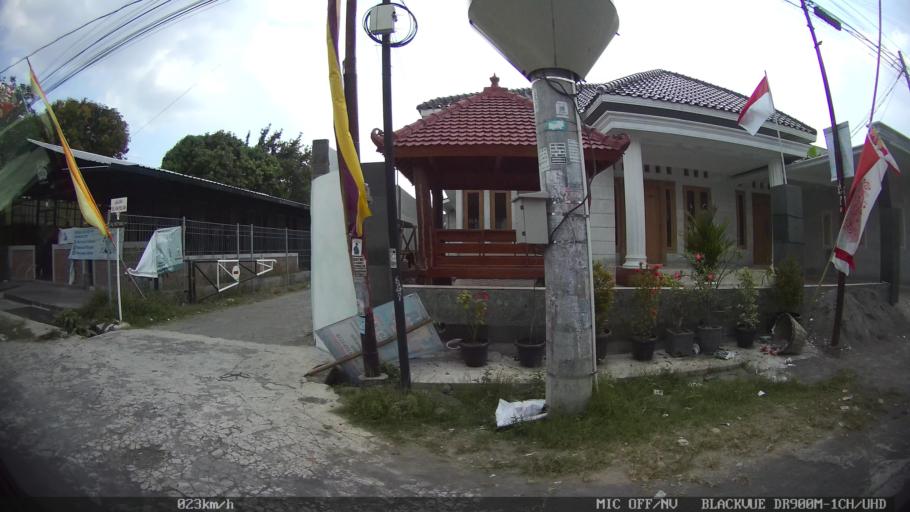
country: ID
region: Daerah Istimewa Yogyakarta
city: Depok
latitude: -7.8030
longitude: 110.4054
